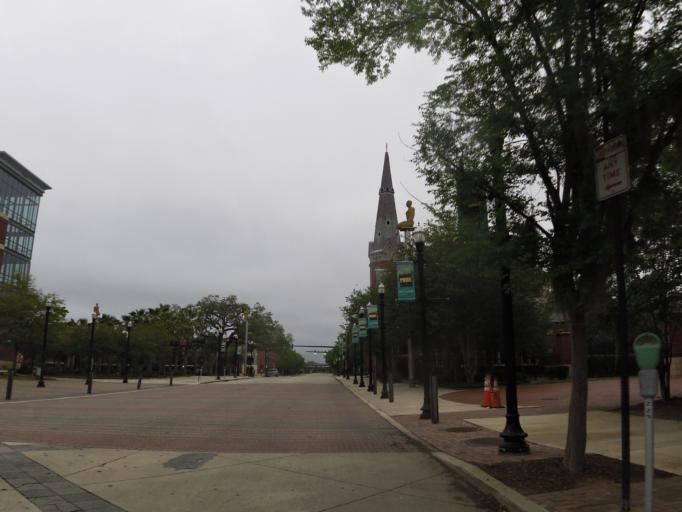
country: US
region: Florida
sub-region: Duval County
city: Jacksonville
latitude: 30.3253
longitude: -81.6439
